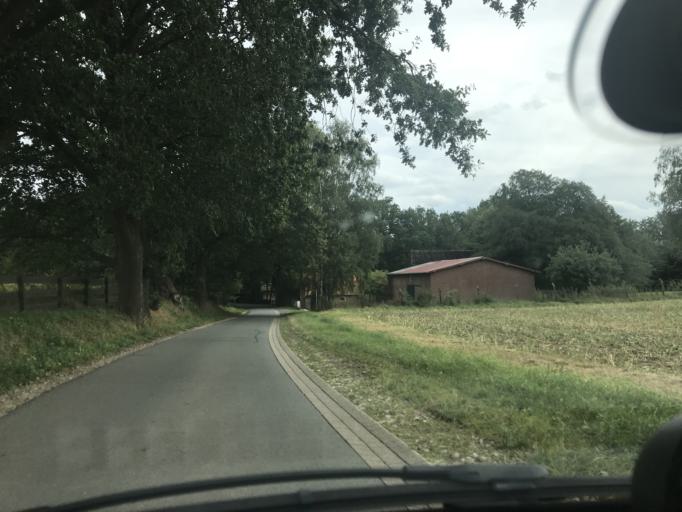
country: DE
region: Lower Saxony
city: Moisburg
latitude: 53.3988
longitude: 9.7205
